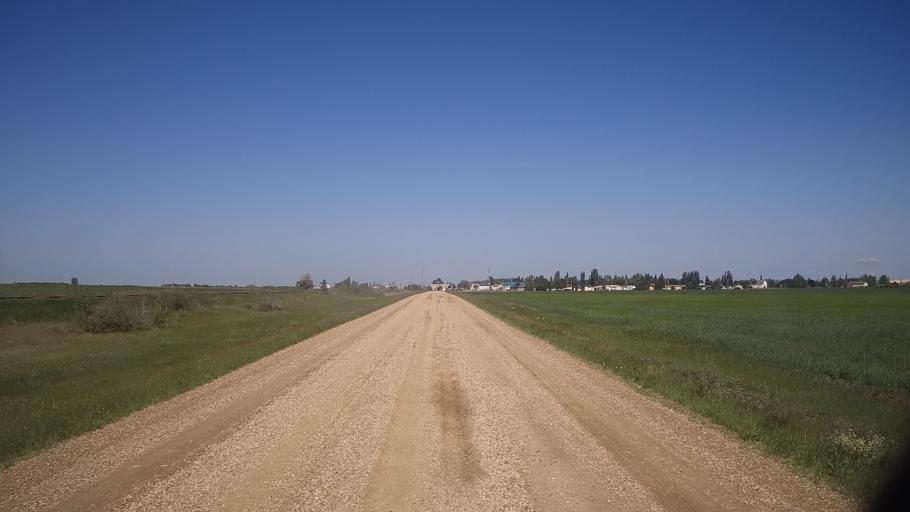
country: CA
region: Saskatchewan
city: Watrous
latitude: 51.8880
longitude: -106.0427
